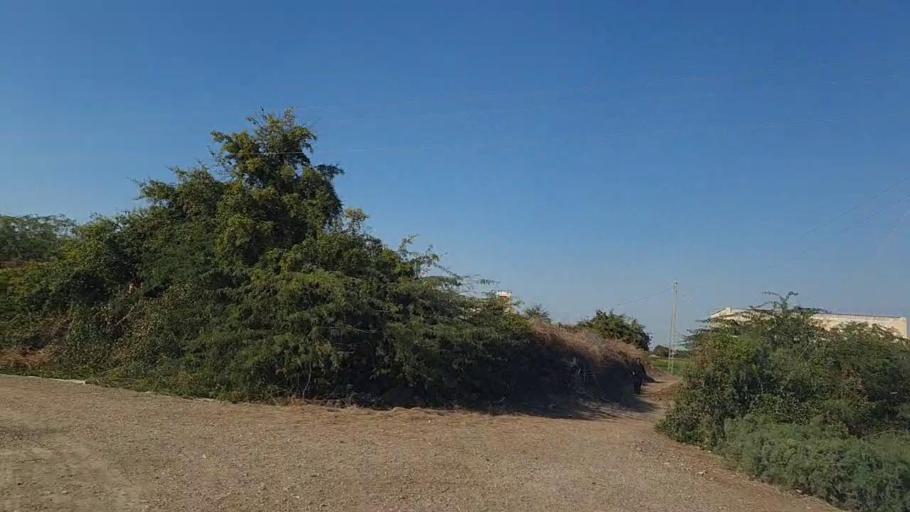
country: PK
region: Sindh
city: Shahpur Chakar
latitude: 26.2227
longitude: 68.6348
